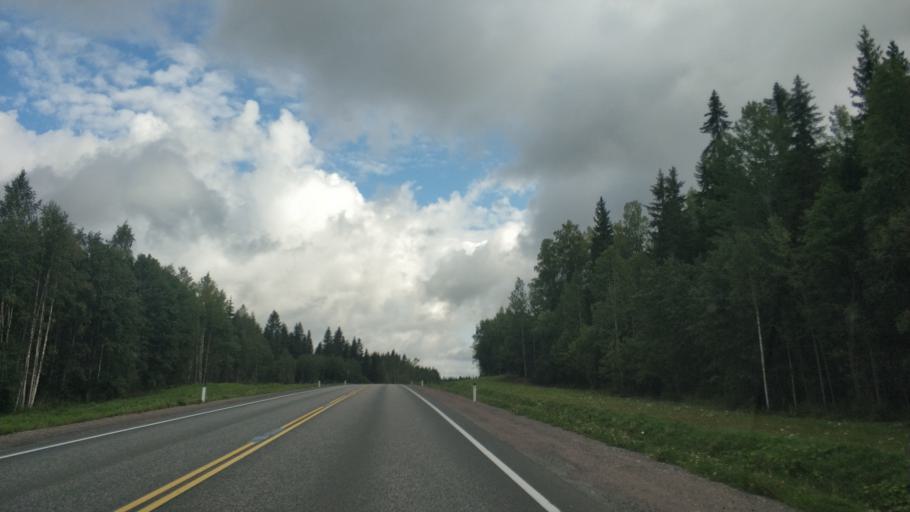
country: RU
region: Republic of Karelia
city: Ruskeala
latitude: 61.8599
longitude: 30.6523
